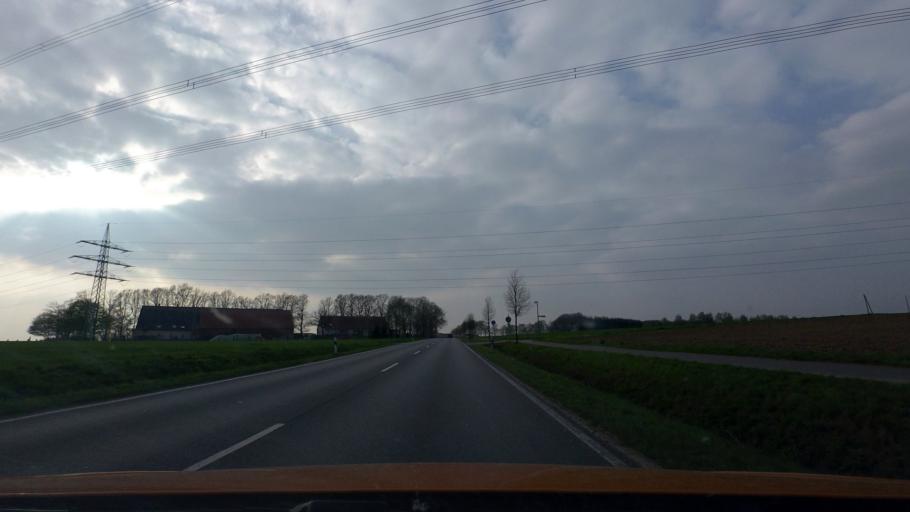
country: DE
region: North Rhine-Westphalia
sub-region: Regierungsbezirk Detmold
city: Hiddenhausen
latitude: 52.1345
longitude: 8.6130
